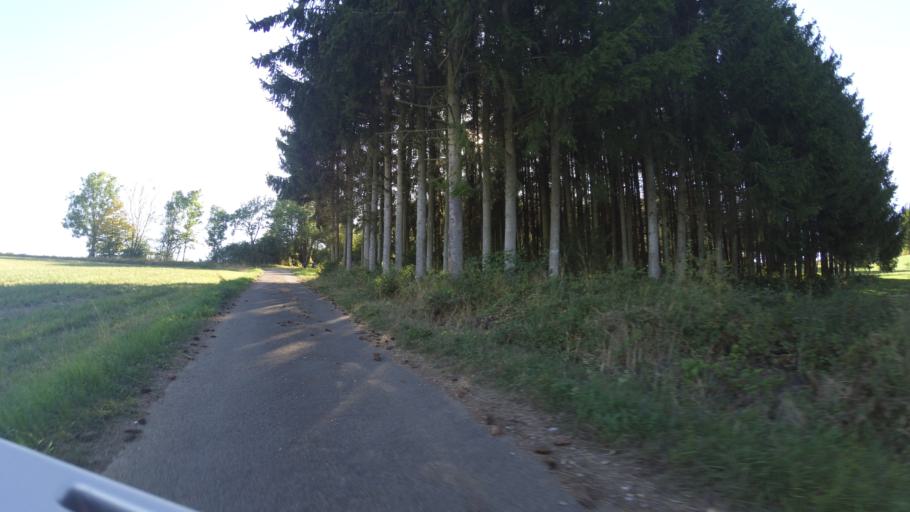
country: DE
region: Saarland
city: Eppelborn
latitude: 49.4490
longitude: 6.9537
